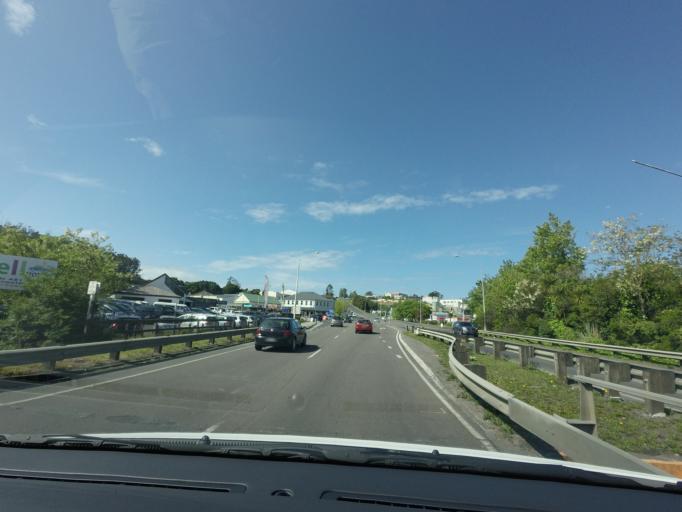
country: NZ
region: Auckland
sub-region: Auckland
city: Rothesay Bay
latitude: -36.6193
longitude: 174.6763
